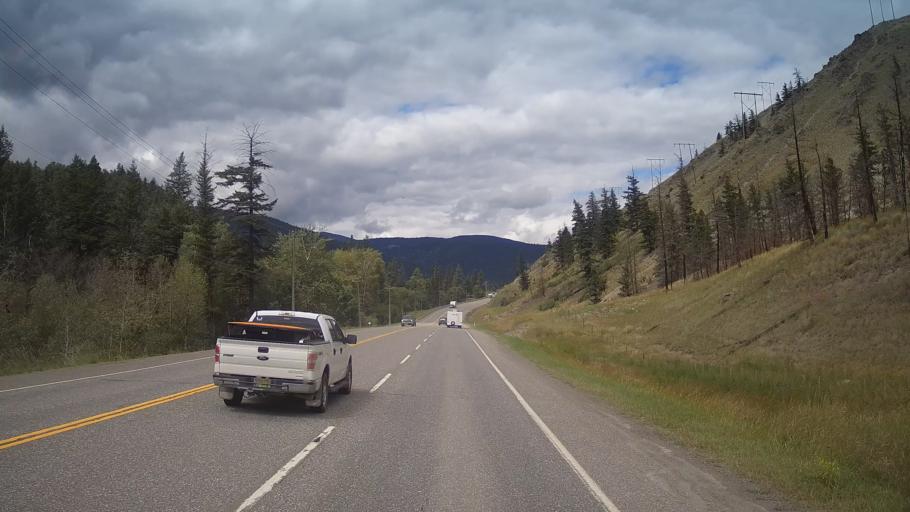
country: CA
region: British Columbia
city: Cache Creek
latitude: 50.9733
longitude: -121.4778
